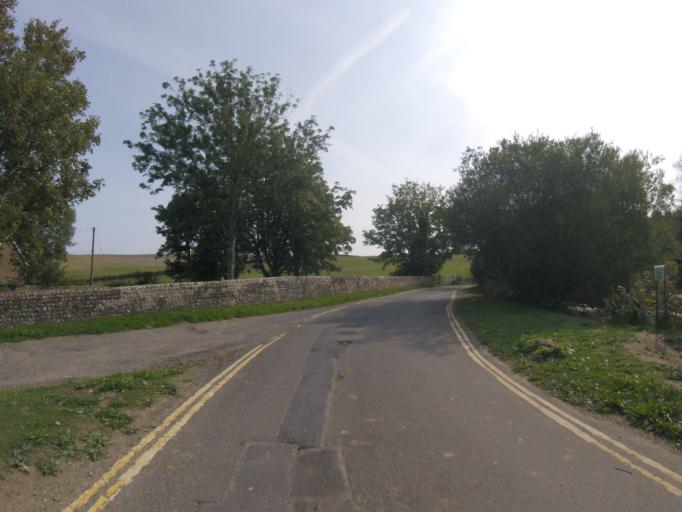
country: GB
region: England
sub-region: Brighton and Hove
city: Rottingdean
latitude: 50.8618
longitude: -0.0763
